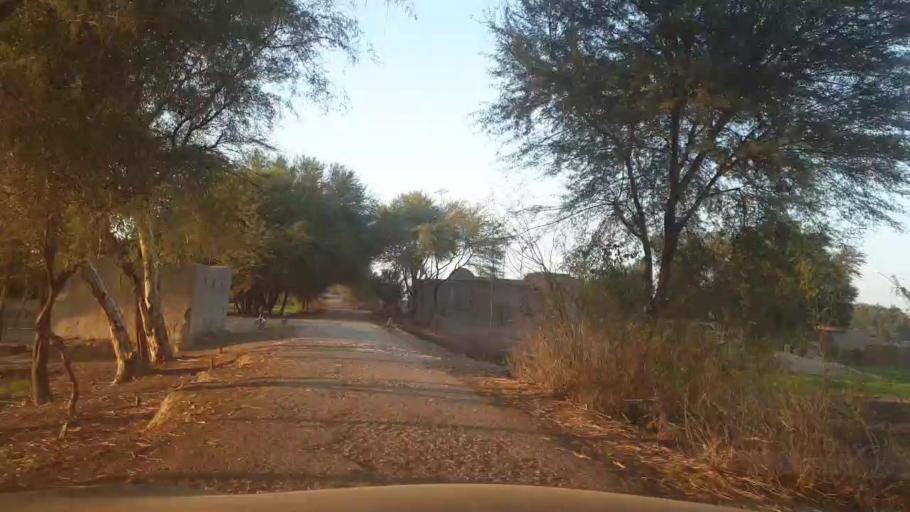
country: PK
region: Sindh
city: Ubauro
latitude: 28.1868
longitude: 69.6019
